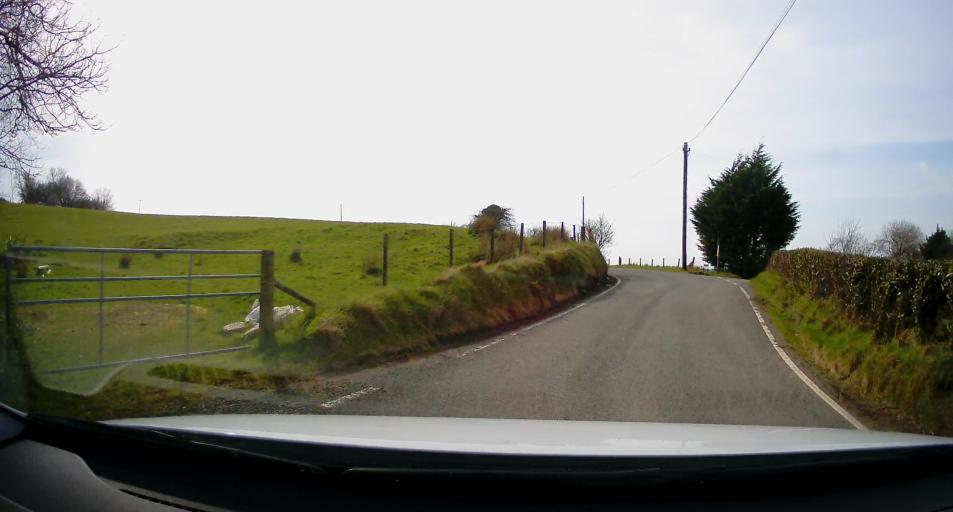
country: GB
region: Wales
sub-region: County of Ceredigion
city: Lledrod
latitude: 52.2569
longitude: -4.0797
